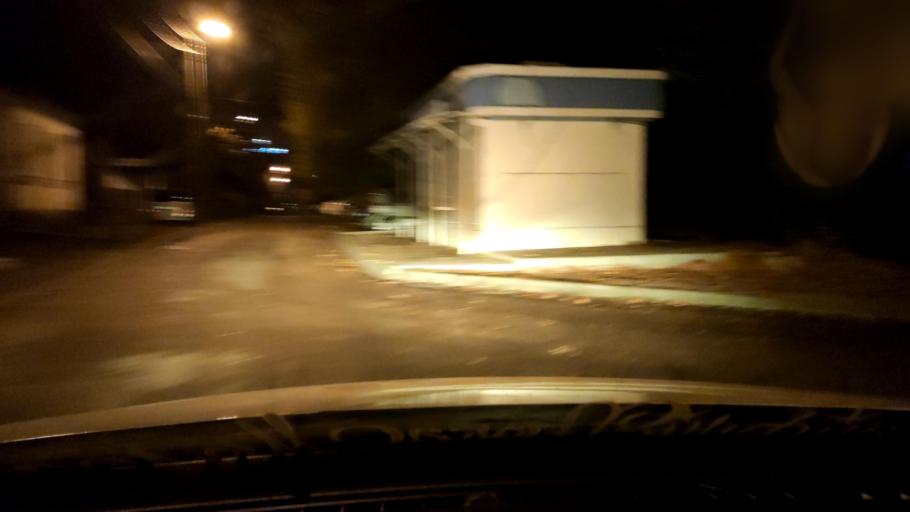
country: RU
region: Voronezj
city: Pridonskoy
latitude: 51.6591
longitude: 39.1193
